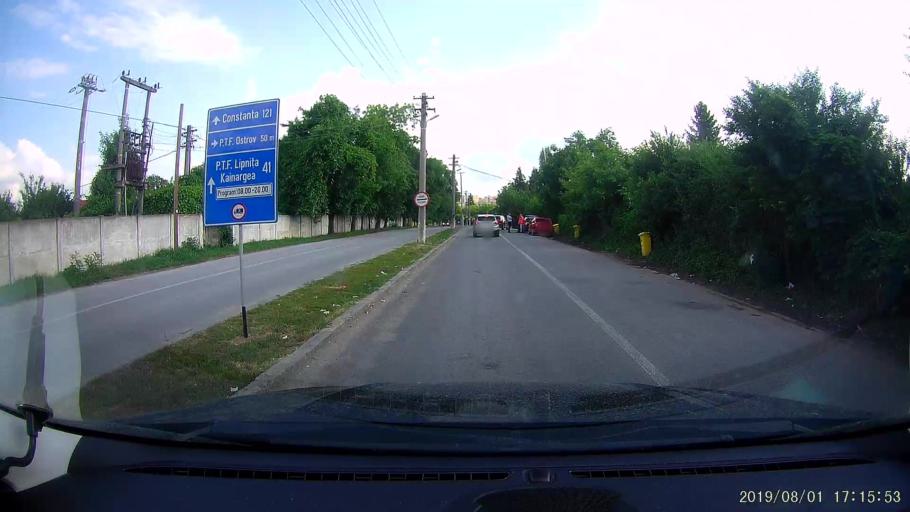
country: BG
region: Silistra
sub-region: Obshtina Silistra
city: Silistra
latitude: 44.1186
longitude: 27.2770
